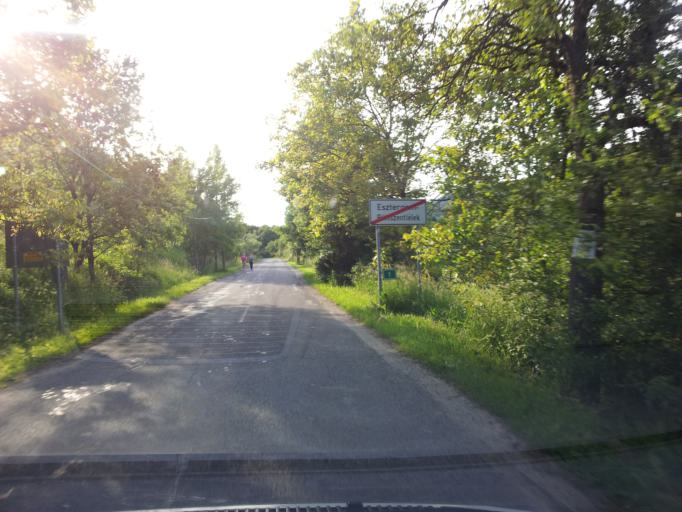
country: HU
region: Komarom-Esztergom
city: Kesztolc
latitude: 47.7311
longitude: 18.8395
